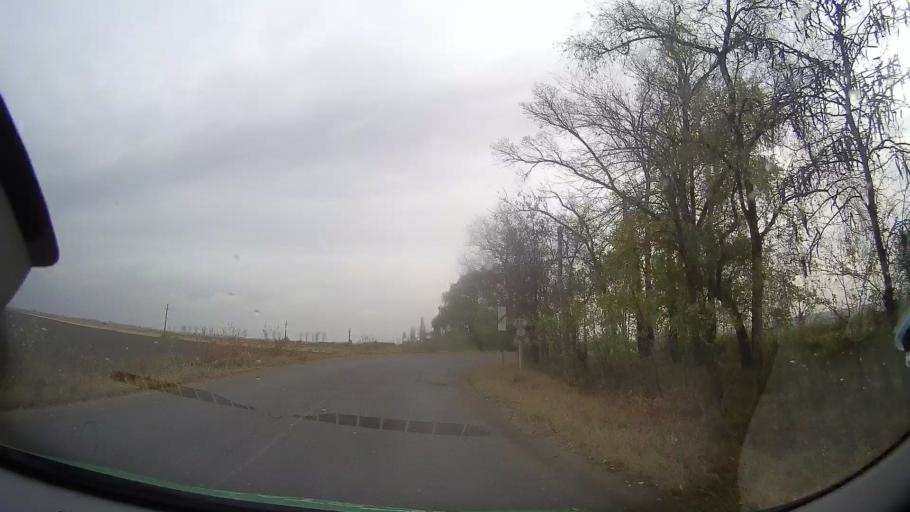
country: RO
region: Prahova
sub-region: Comuna Dumbrava
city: Dumbrava
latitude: 44.8619
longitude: 26.2073
